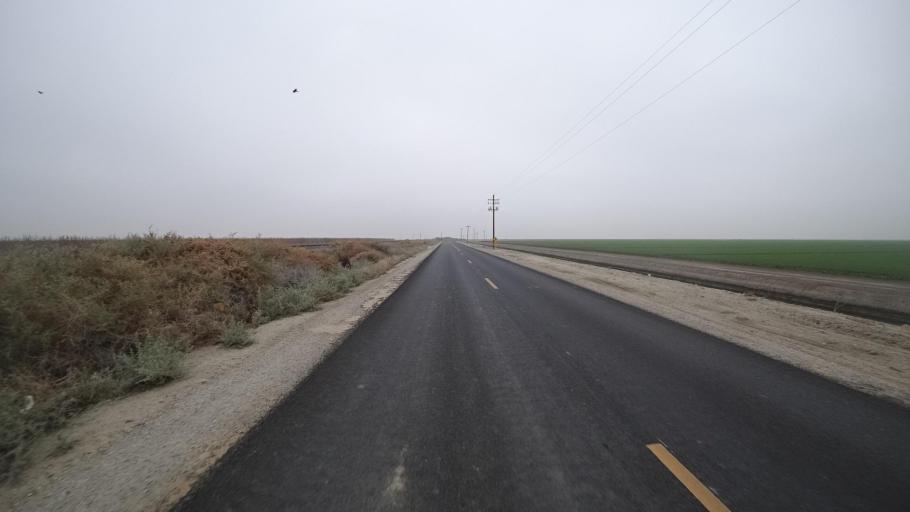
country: US
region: California
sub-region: Kern County
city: Greenfield
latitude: 35.1801
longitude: -119.1861
